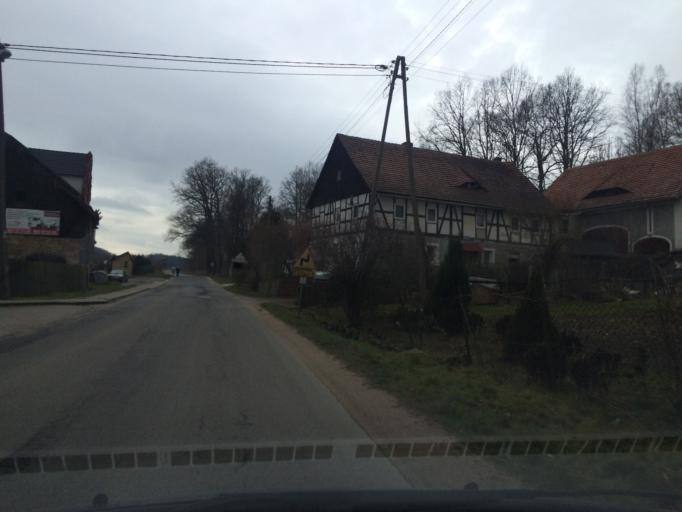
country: PL
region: Lower Silesian Voivodeship
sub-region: Powiat lwowecki
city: Lwowek Slaski
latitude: 51.1209
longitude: 15.5417
